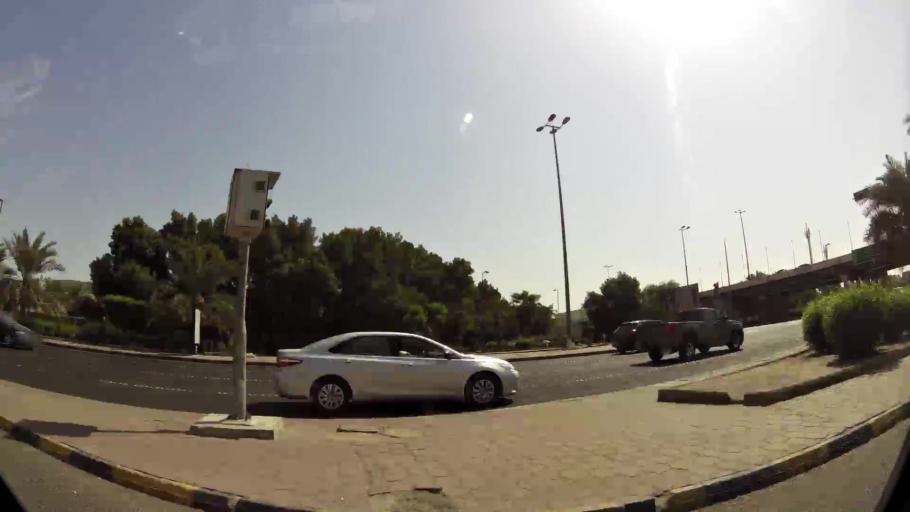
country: KW
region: Al Asimah
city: Ad Dasmah
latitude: 29.3664
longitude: 48.0110
